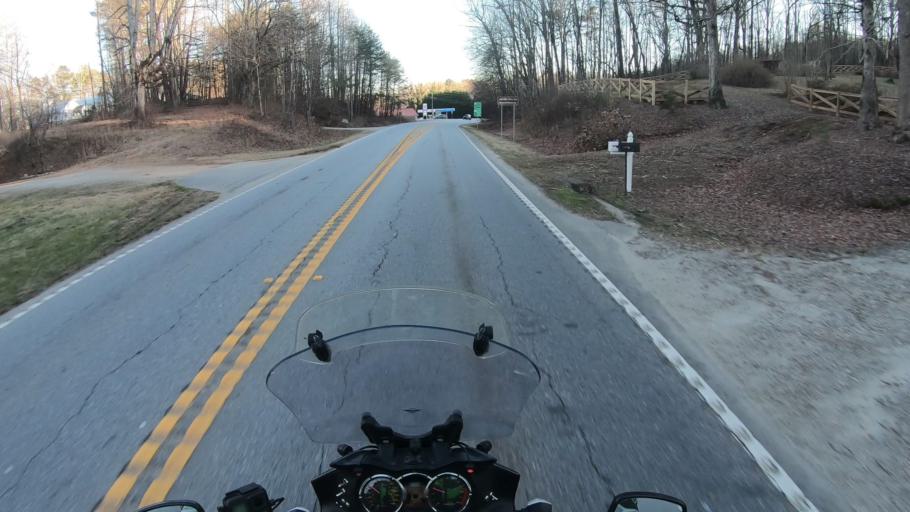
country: US
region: Georgia
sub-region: Lumpkin County
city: Dahlonega
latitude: 34.5642
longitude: -83.9705
